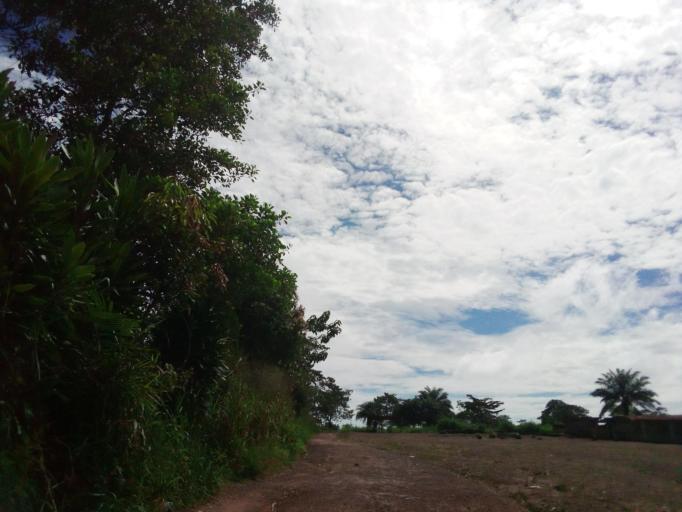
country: SL
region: Eastern Province
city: Koidu
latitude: 8.6535
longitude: -10.9585
